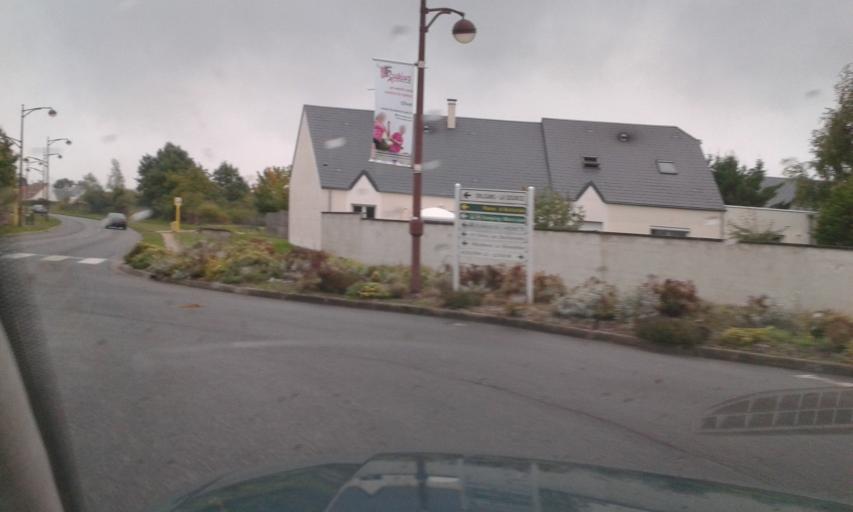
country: FR
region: Centre
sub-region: Departement du Loiret
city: Olivet
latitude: 47.8557
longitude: 1.8987
